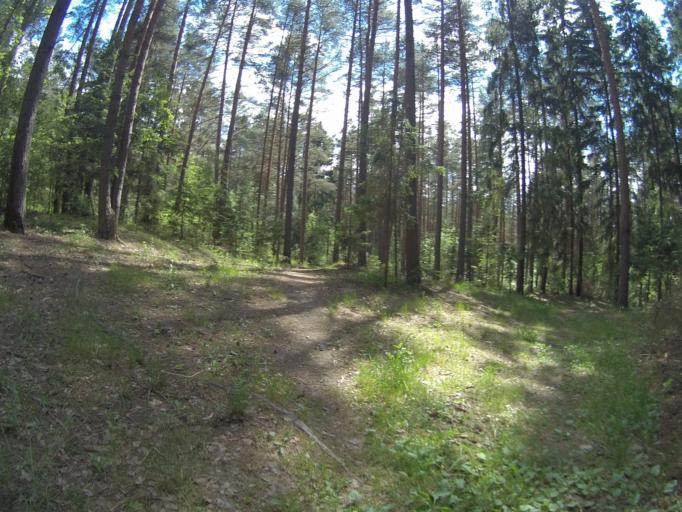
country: RU
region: Vladimir
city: Raduzhnyy
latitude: 56.0077
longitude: 40.2780
